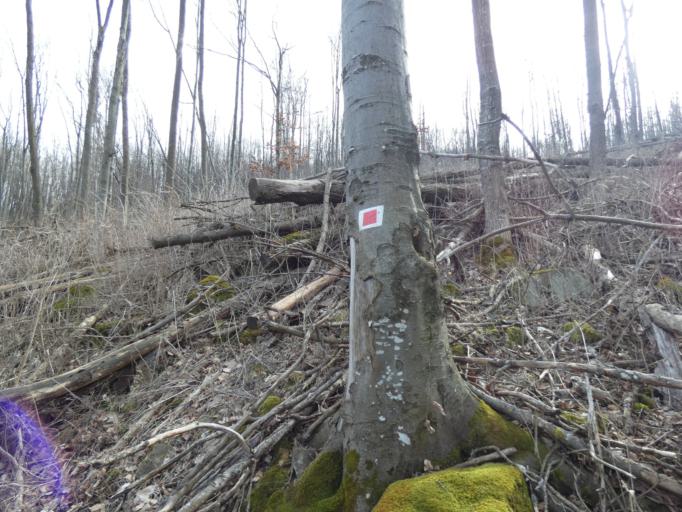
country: HU
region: Nograd
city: Diosjeno
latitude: 47.9594
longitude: 18.9445
